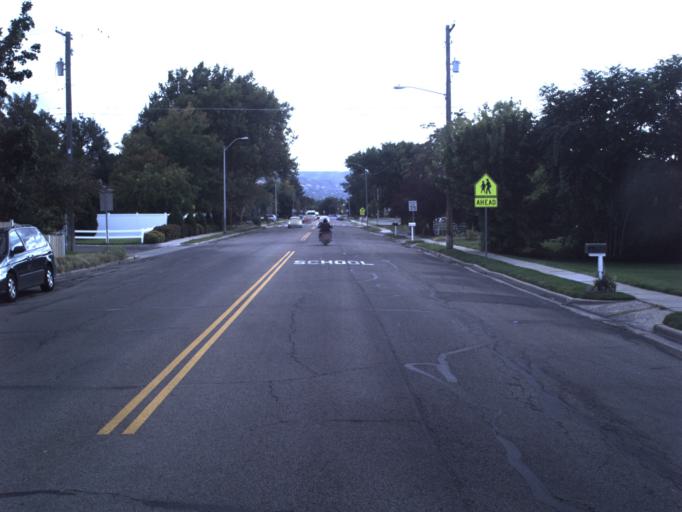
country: US
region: Utah
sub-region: Davis County
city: Bountiful
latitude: 40.8978
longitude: -111.8790
